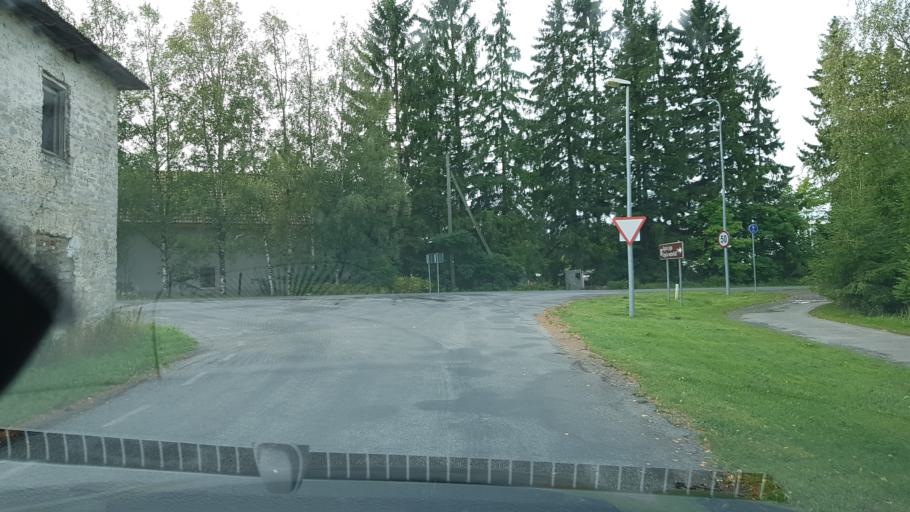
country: EE
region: Harju
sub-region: Raasiku vald
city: Raasiku
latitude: 59.4413
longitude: 25.1699
